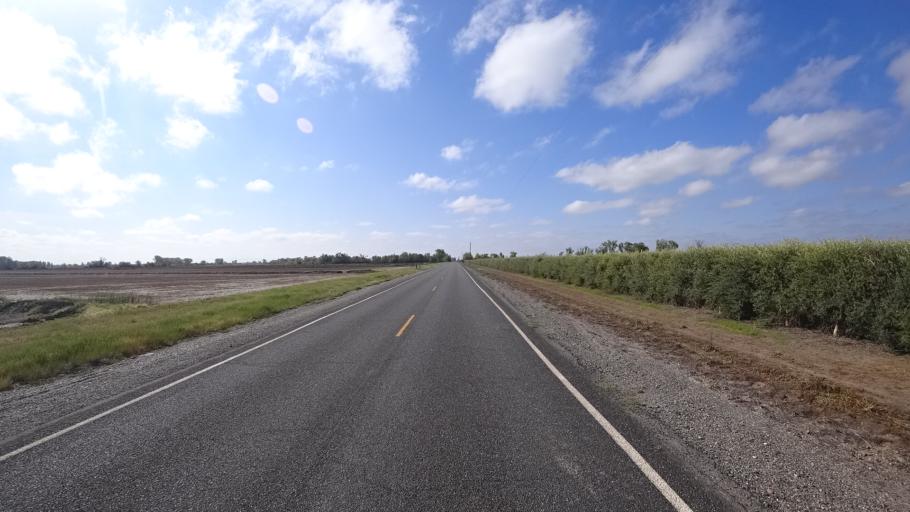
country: US
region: California
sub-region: Butte County
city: Durham
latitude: 39.4731
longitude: -121.9301
